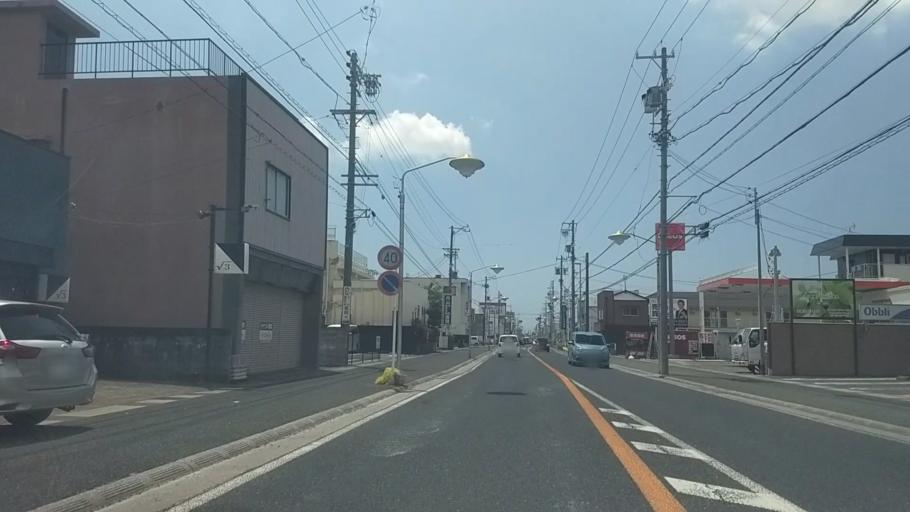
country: JP
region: Shizuoka
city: Hamamatsu
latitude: 34.7464
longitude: 137.7242
